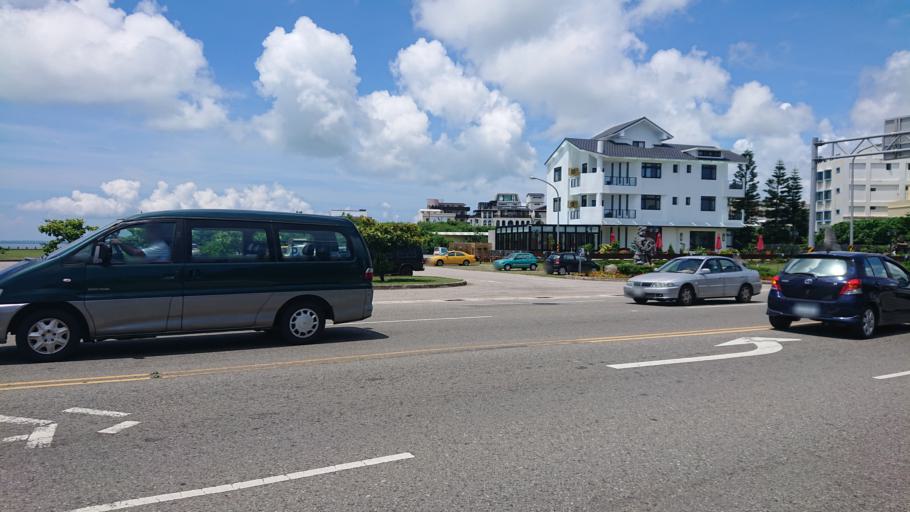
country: TW
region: Taiwan
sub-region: Penghu
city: Ma-kung
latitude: 23.5688
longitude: 119.5975
